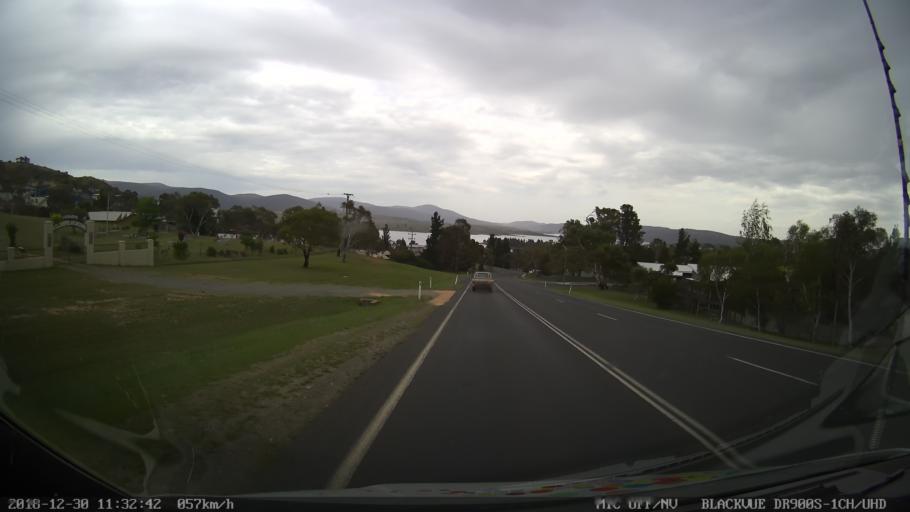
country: AU
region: New South Wales
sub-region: Snowy River
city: Jindabyne
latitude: -36.4199
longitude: 148.6104
